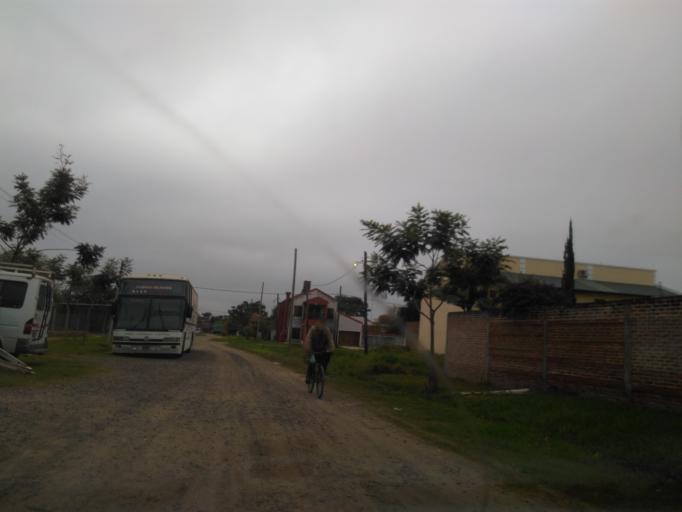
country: AR
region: Chaco
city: Fontana
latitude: -27.4424
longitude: -59.0235
